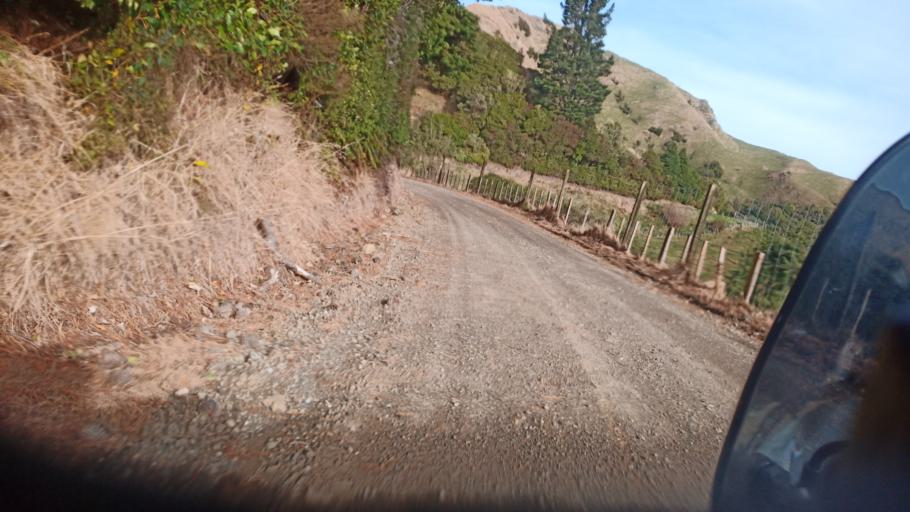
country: NZ
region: Gisborne
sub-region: Gisborne District
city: Gisborne
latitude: -38.4581
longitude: 177.5387
